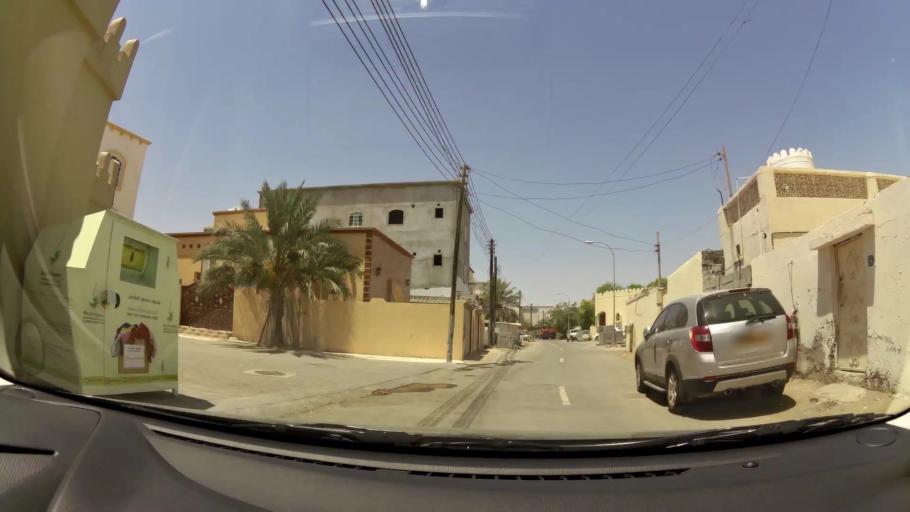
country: OM
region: Muhafazat Masqat
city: As Sib al Jadidah
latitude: 23.6268
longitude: 58.2404
